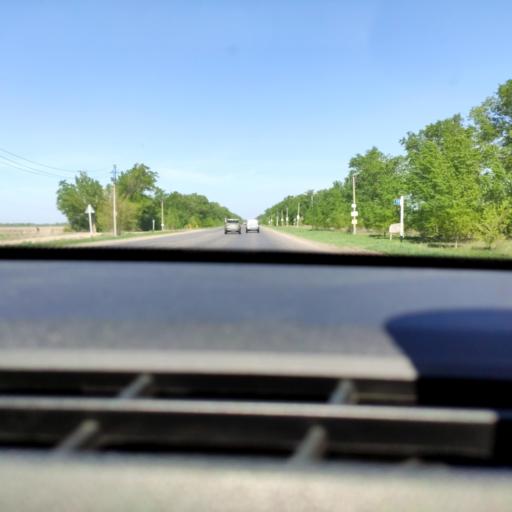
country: RU
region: Samara
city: Tol'yatti
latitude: 53.5878
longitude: 49.4055
